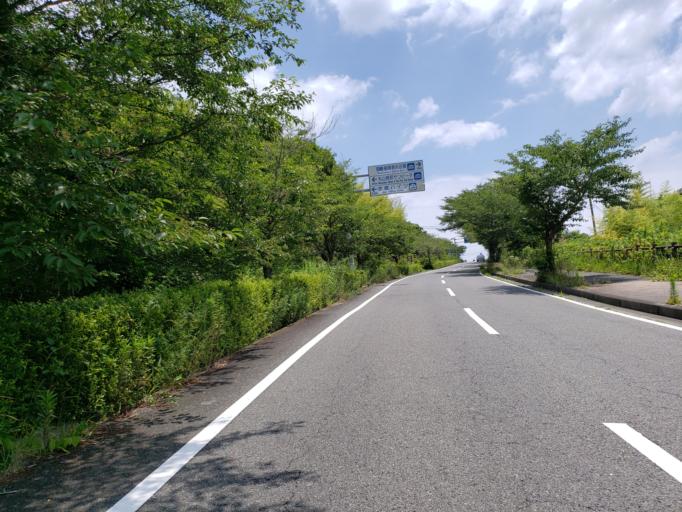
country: JP
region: Hyogo
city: Kariya
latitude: 34.7368
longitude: 134.4160
